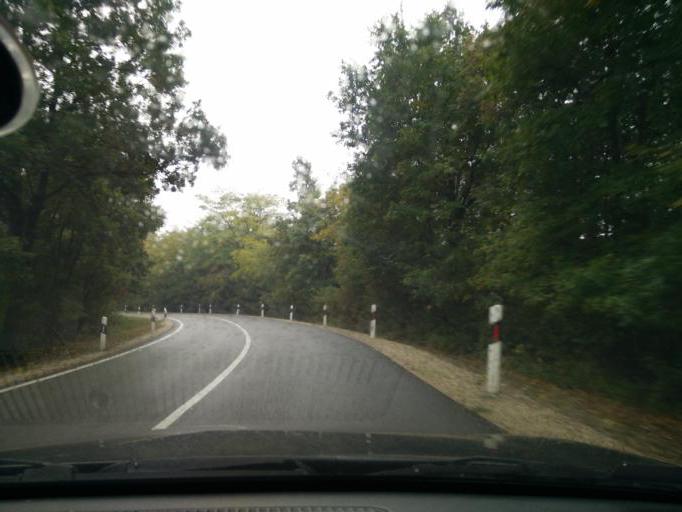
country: HU
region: Komarom-Esztergom
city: Tarjan
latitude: 47.6348
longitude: 18.5492
